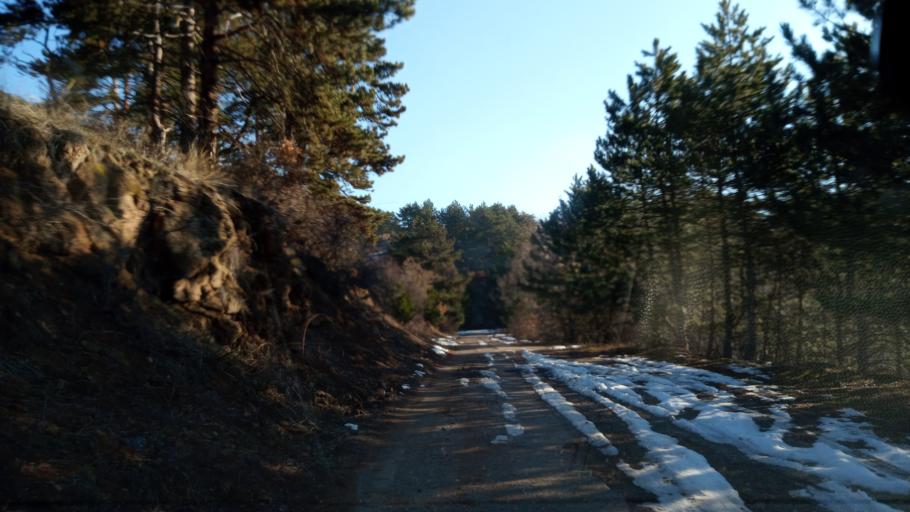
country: BG
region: Sofia-Capital
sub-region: Stolichna Obshtina
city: Bukhovo
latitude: 42.7952
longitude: 23.5293
